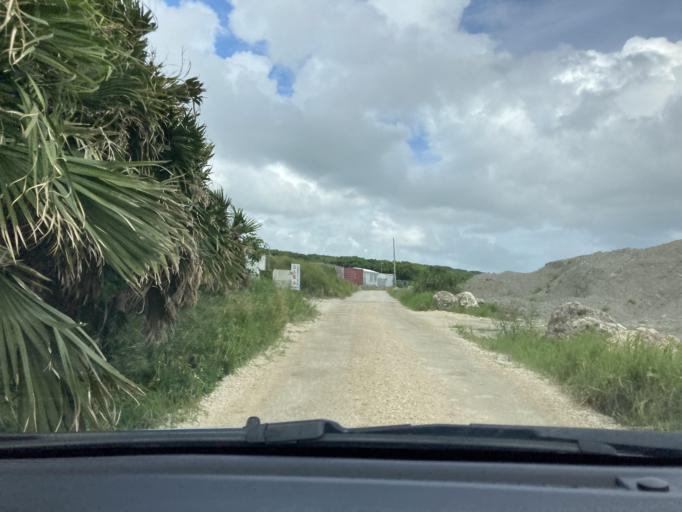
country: JP
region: Okinawa
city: Itoman
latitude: 26.0809
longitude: 127.6839
